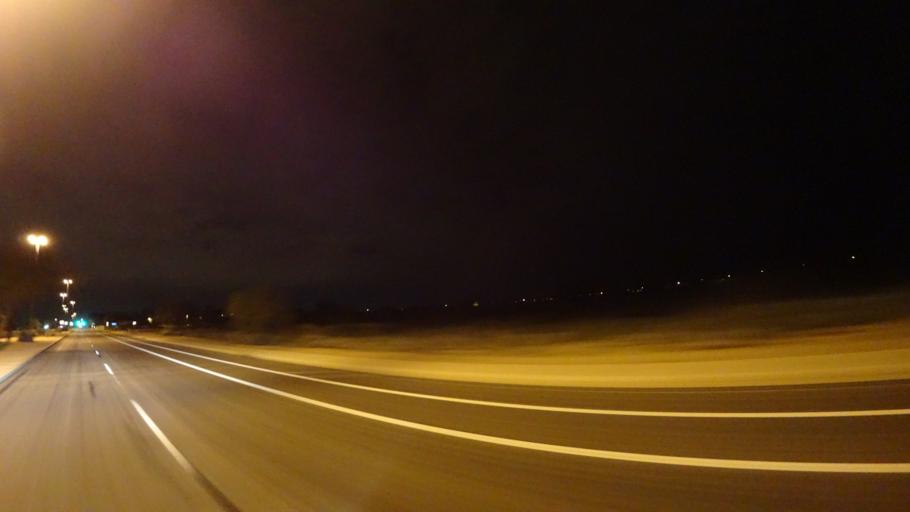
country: US
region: Arizona
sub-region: Pinal County
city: Apache Junction
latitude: 33.4370
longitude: -111.6649
